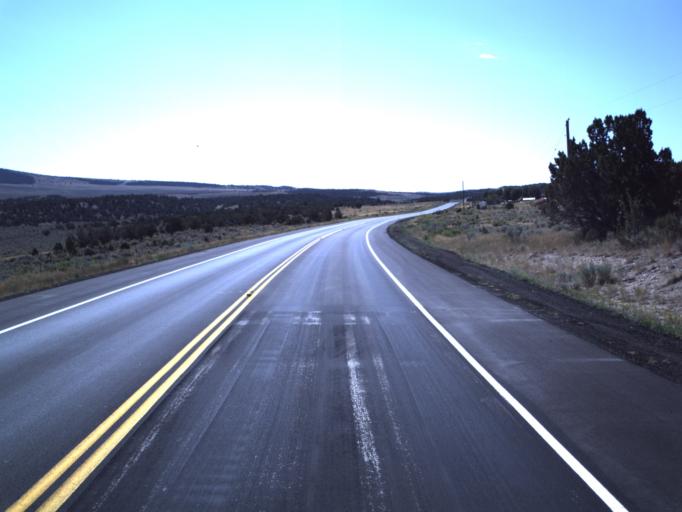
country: US
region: Utah
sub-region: Utah County
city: Eagle Mountain
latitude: 40.0314
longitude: -112.2844
